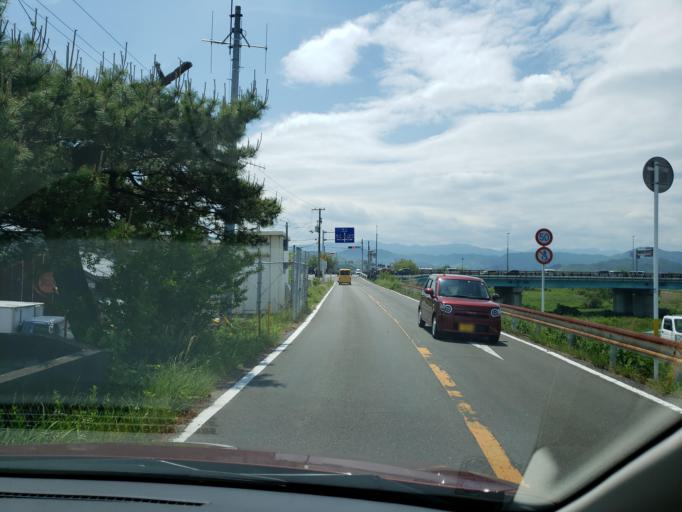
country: JP
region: Tokushima
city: Ishii
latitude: 34.0735
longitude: 134.5004
